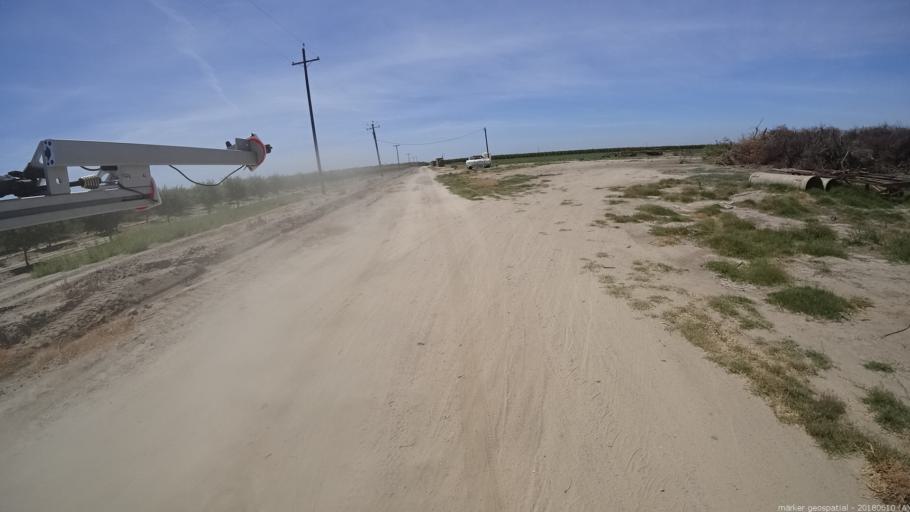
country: US
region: California
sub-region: Madera County
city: Chowchilla
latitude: 37.0434
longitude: -120.4193
